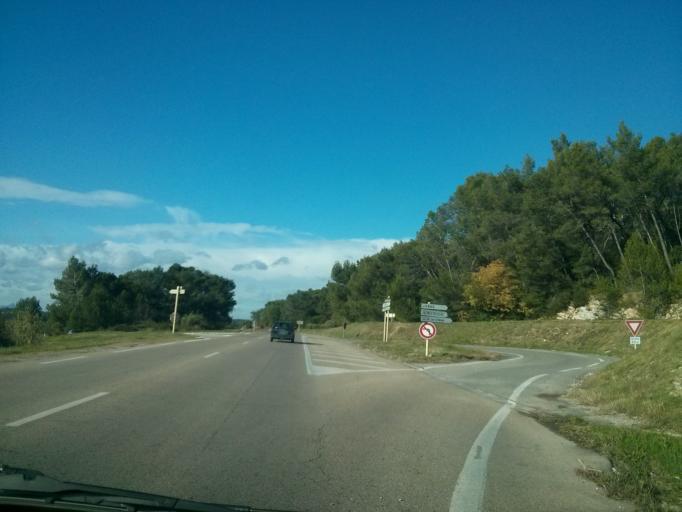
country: FR
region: Languedoc-Roussillon
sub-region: Departement du Gard
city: Congenies
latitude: 43.7748
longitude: 4.1503
